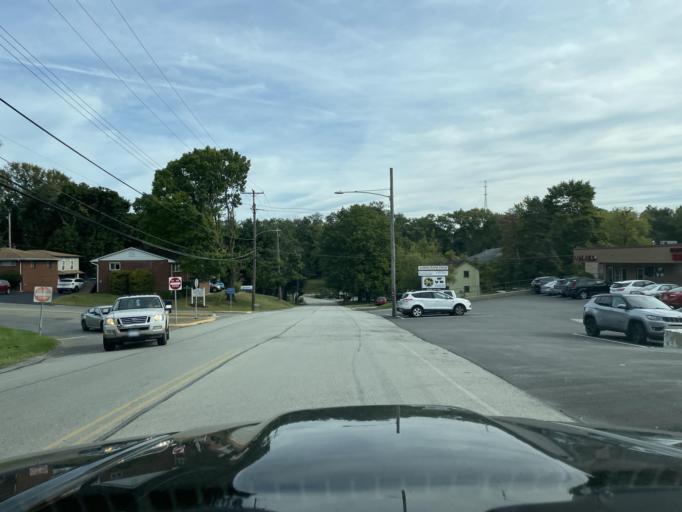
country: US
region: Pennsylvania
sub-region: Allegheny County
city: Monroeville
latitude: 40.4404
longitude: -79.7678
